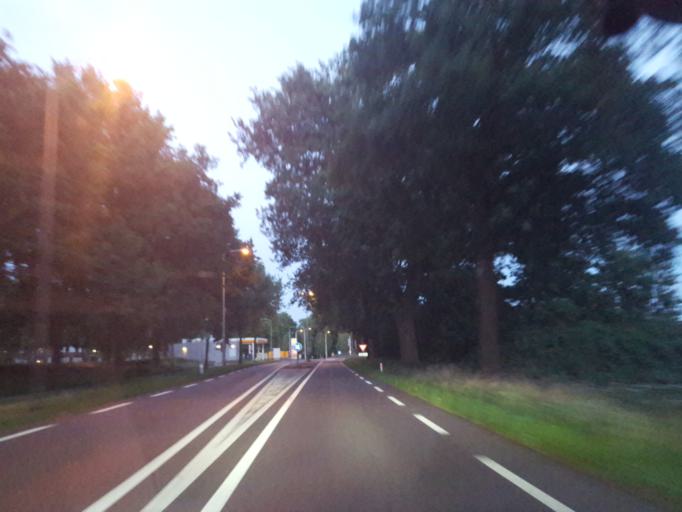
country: NL
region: Limburg
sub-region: Gemeente Leudal
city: Heythuysen
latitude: 51.3445
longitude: 5.8781
